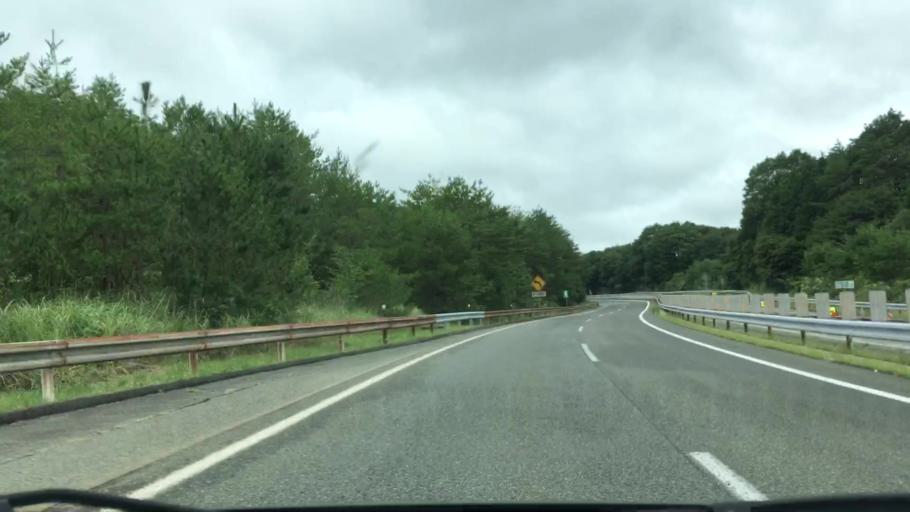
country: JP
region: Hiroshima
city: Shobara
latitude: 34.8716
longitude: 133.1566
